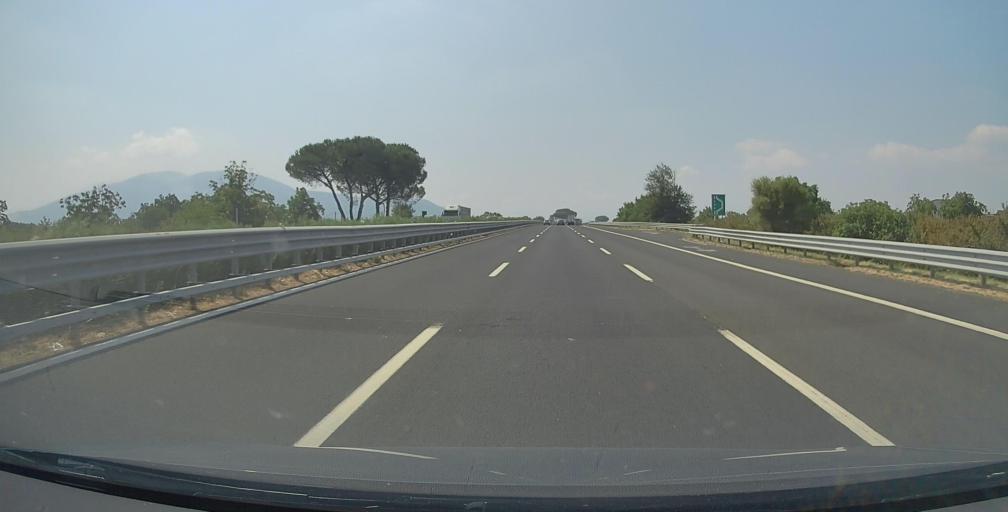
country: IT
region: Campania
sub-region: Provincia di Napoli
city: Piazzolla
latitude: 40.9015
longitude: 14.5317
